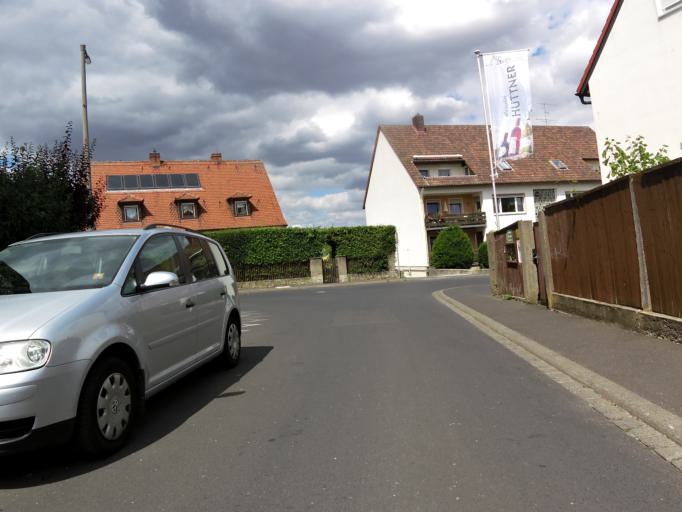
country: DE
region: Bavaria
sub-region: Regierungsbezirk Unterfranken
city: Gerbrunn
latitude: 49.7798
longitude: 9.9787
